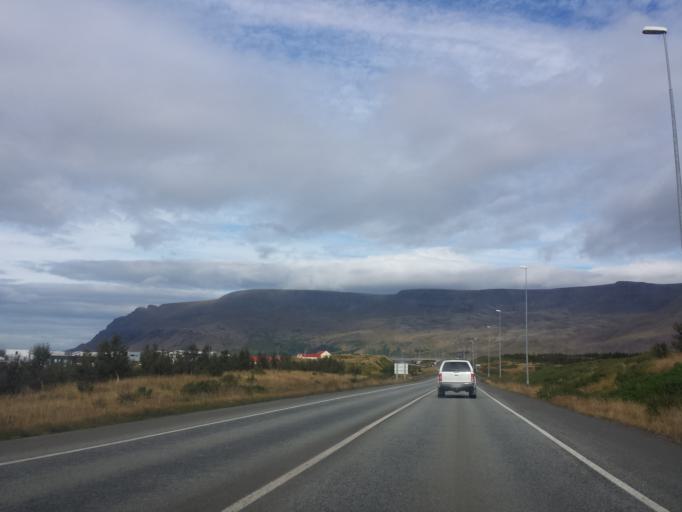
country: IS
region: Capital Region
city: Mosfellsbaer
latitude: 64.1785
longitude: -21.6777
